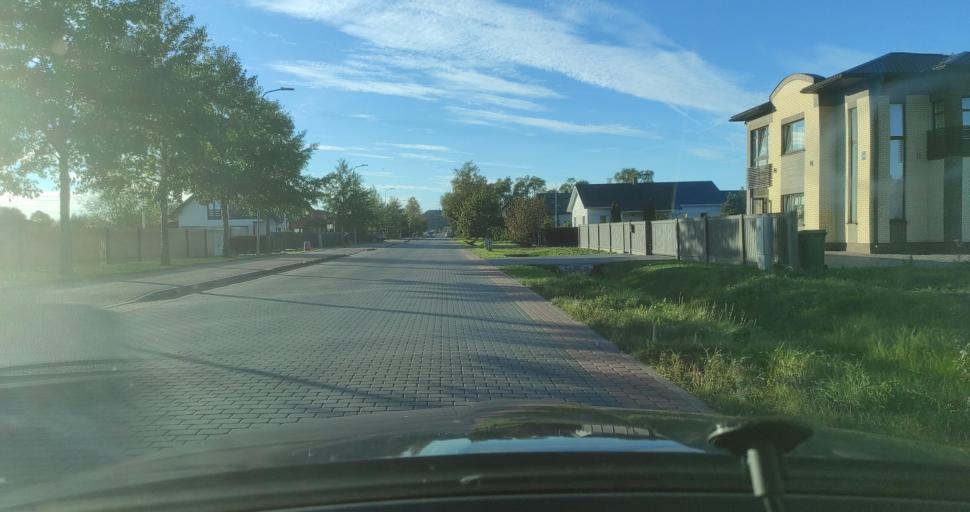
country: LV
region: Ventspils
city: Ventspils
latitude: 57.3661
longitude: 21.5709
